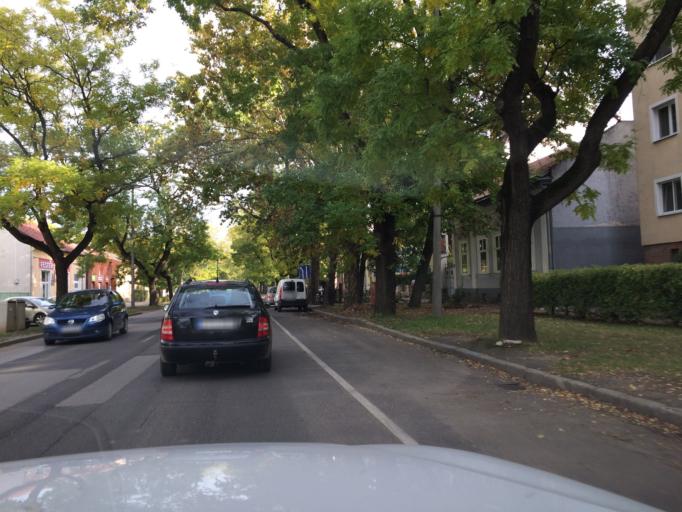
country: HU
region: Szabolcs-Szatmar-Bereg
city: Nyiregyhaza
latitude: 47.9561
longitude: 21.7058
